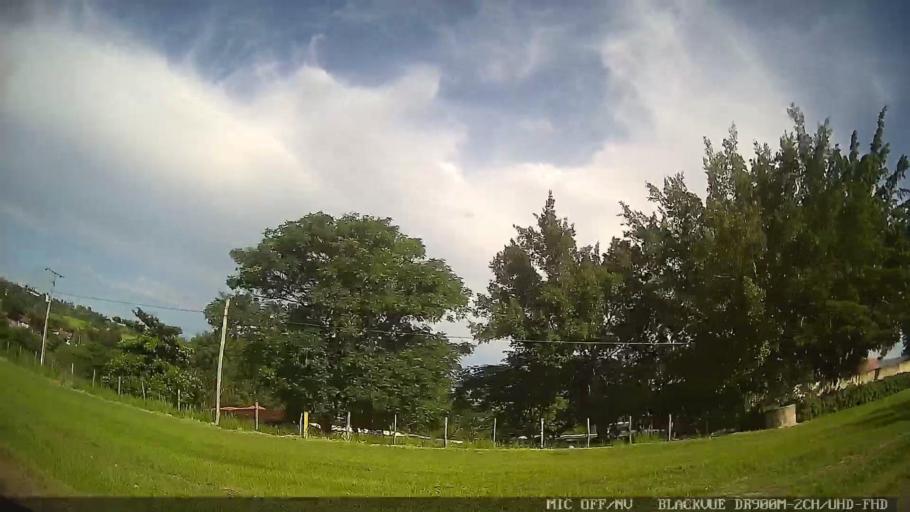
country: BR
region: Sao Paulo
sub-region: Tiete
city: Tiete
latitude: -23.1122
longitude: -47.6969
